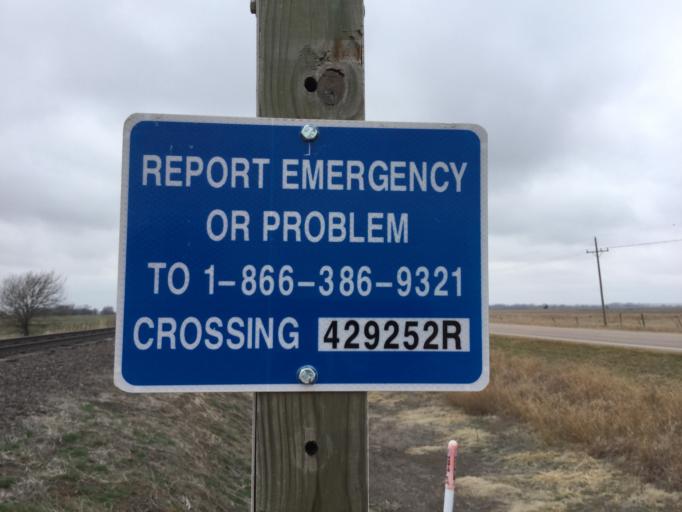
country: US
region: Kansas
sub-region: Barton County
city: Hoisington
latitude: 38.5218
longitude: -98.6830
